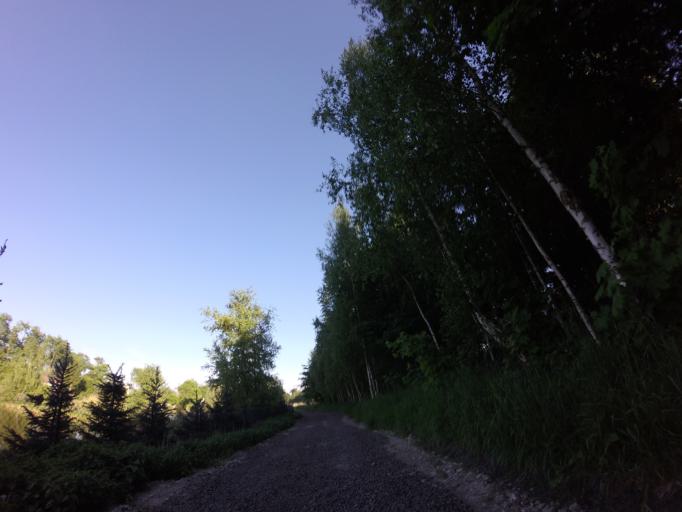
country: PL
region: West Pomeranian Voivodeship
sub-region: Powiat choszczenski
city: Choszczno
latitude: 53.1468
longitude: 15.4337
